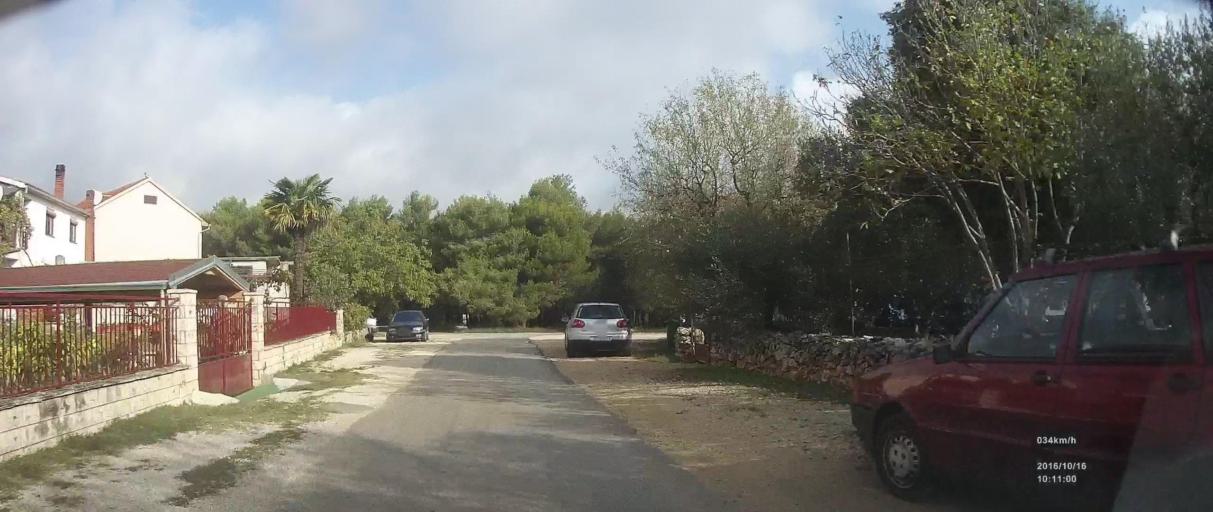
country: HR
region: Zadarska
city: Pakostane
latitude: 43.9143
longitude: 15.5073
